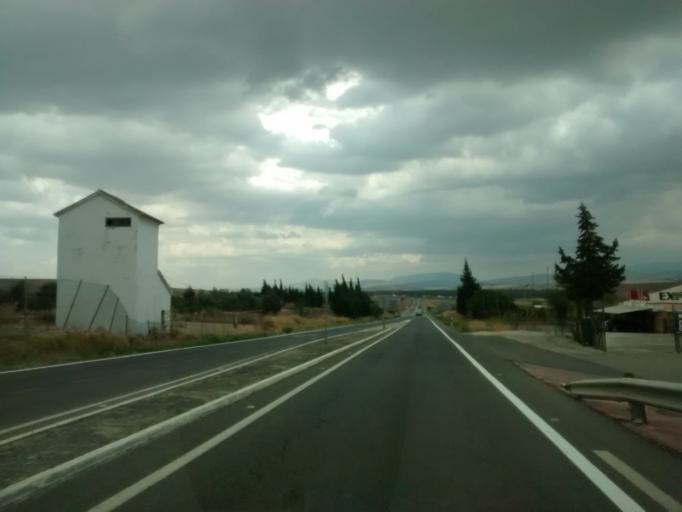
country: ES
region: Andalusia
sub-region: Provincia de Cadiz
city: Bornos
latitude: 36.8248
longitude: -5.7418
